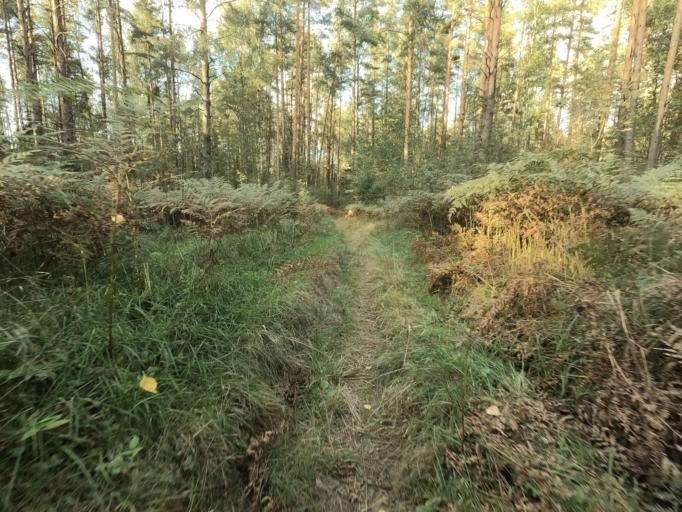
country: RU
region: Leningrad
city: Imeni Sverdlova
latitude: 59.8504
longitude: 30.7281
